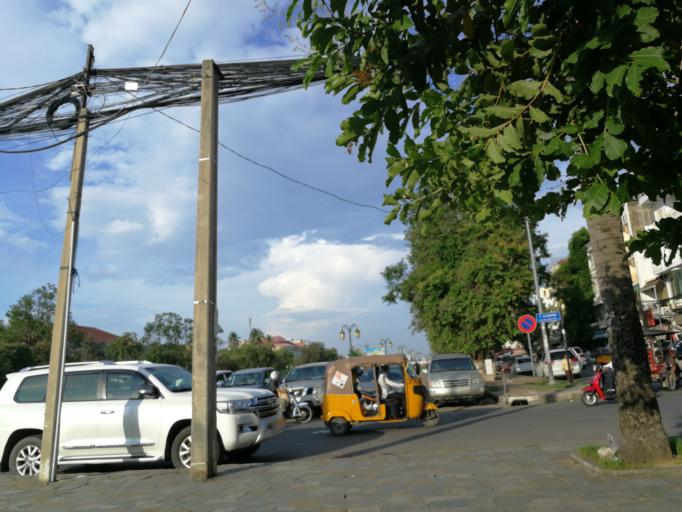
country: KH
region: Phnom Penh
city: Phnom Penh
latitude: 11.5734
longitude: 104.9244
